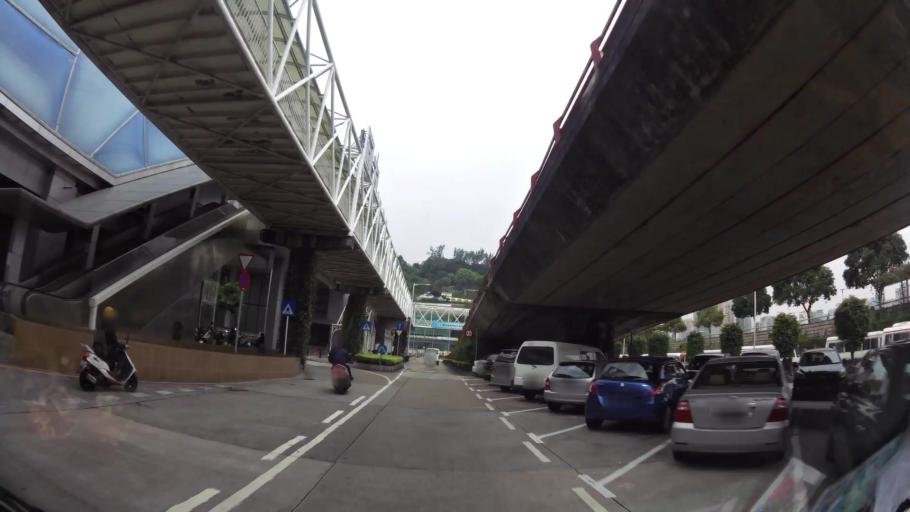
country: MO
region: Macau
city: Macau
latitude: 22.1975
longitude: 113.5559
